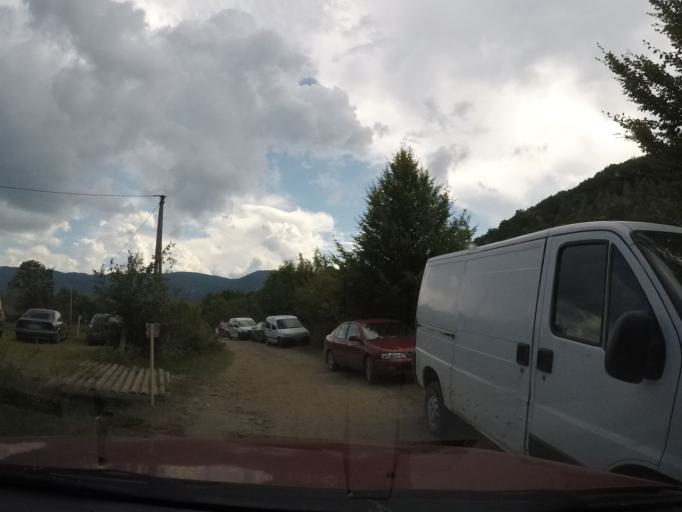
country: UA
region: Zakarpattia
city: Velykyi Bereznyi
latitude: 49.0415
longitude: 22.5813
